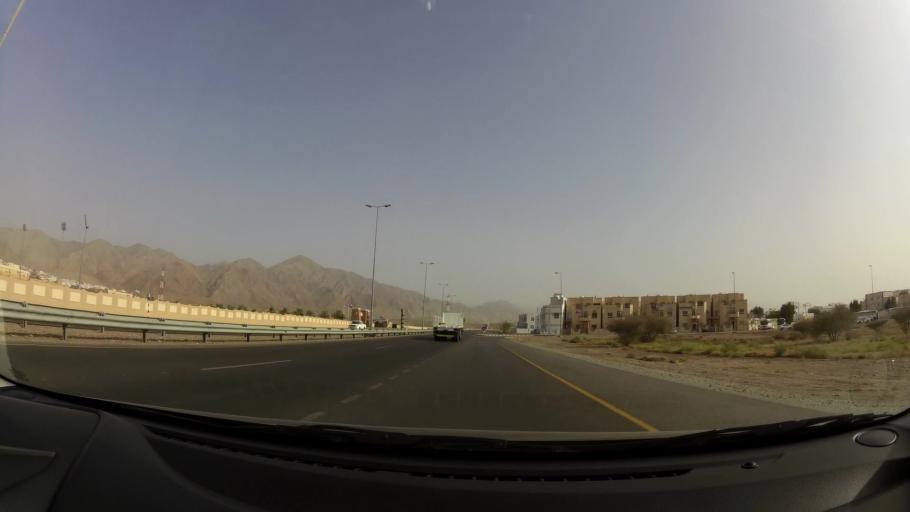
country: OM
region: Muhafazat Masqat
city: Bawshar
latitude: 23.5476
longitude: 58.3661
